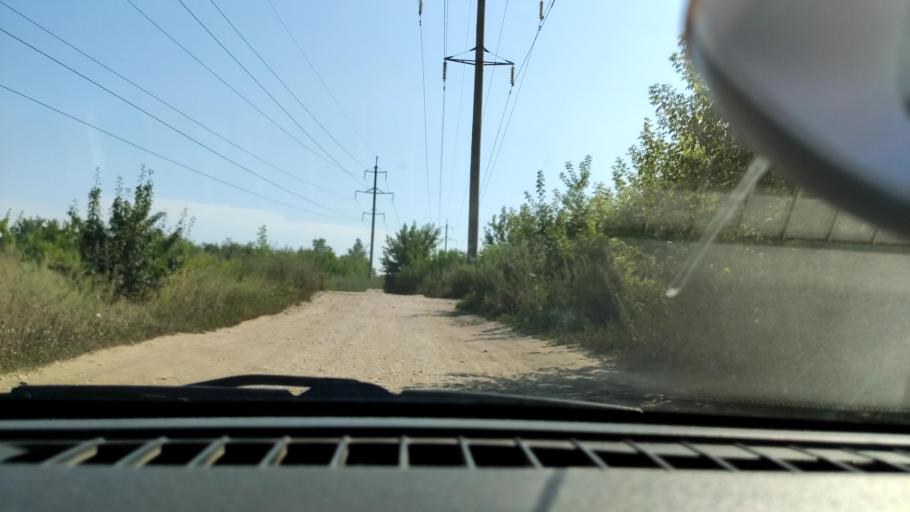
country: RU
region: Samara
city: Petra-Dubrava
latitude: 53.2680
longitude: 50.3015
